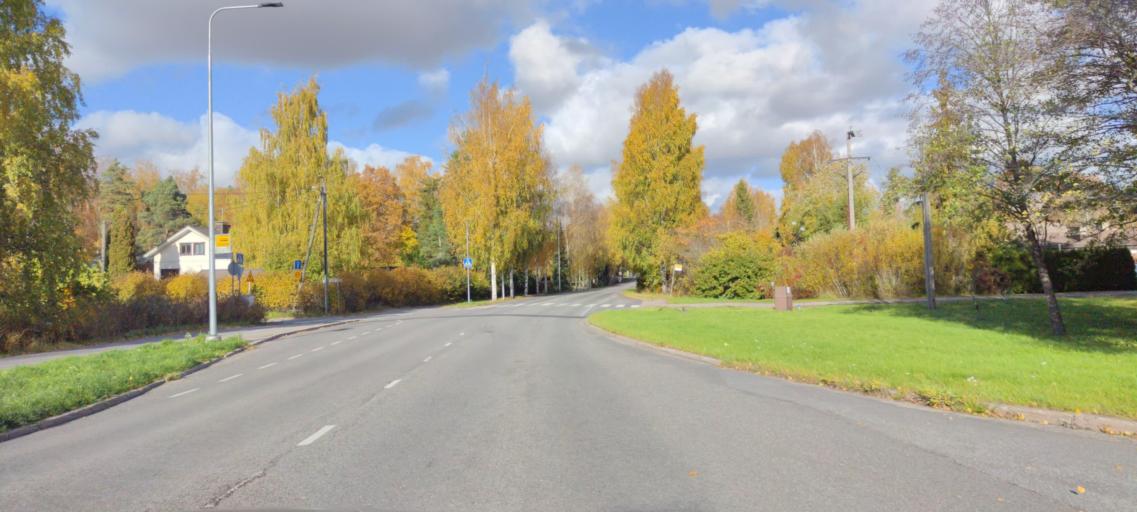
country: FI
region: Varsinais-Suomi
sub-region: Turku
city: Turku
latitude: 60.4182
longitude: 22.2695
